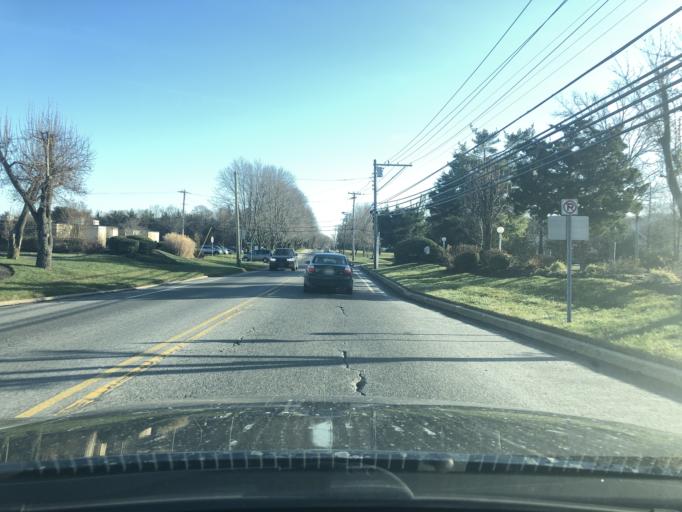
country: US
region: New Jersey
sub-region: Atlantic County
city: Northfield
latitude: 39.3922
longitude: -74.5515
